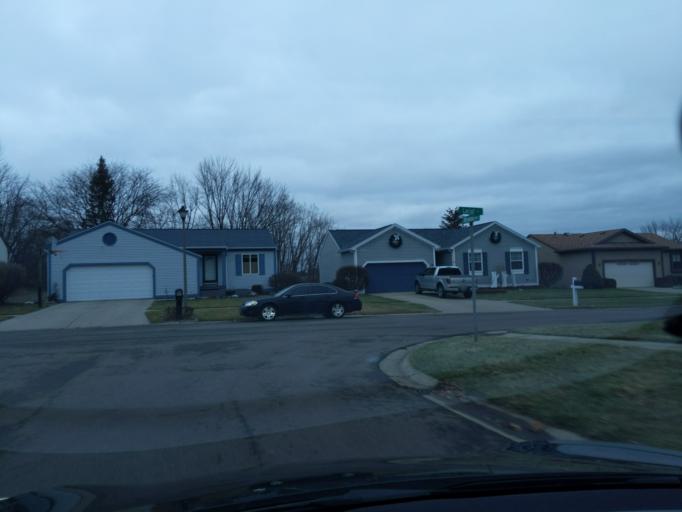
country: US
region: Michigan
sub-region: Eaton County
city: Waverly
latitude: 42.7385
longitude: -84.6121
